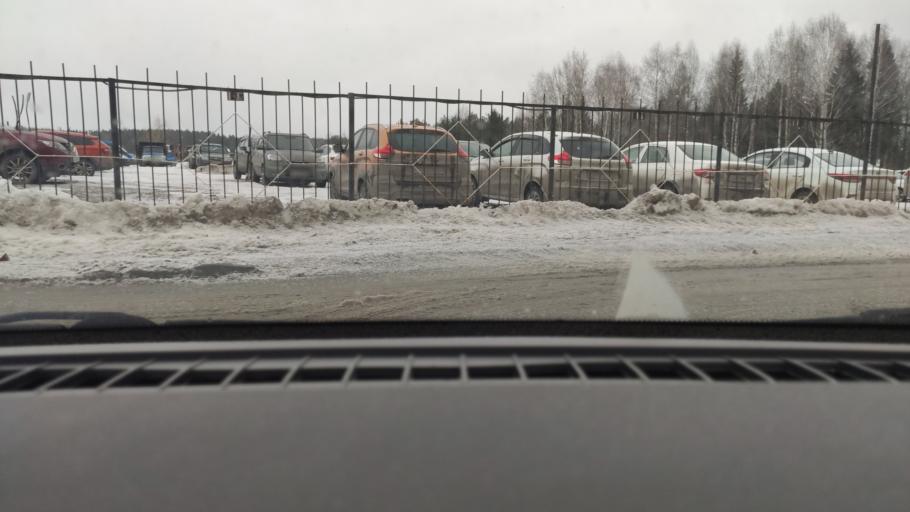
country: RU
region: Perm
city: Polazna
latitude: 58.1347
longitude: 56.4016
